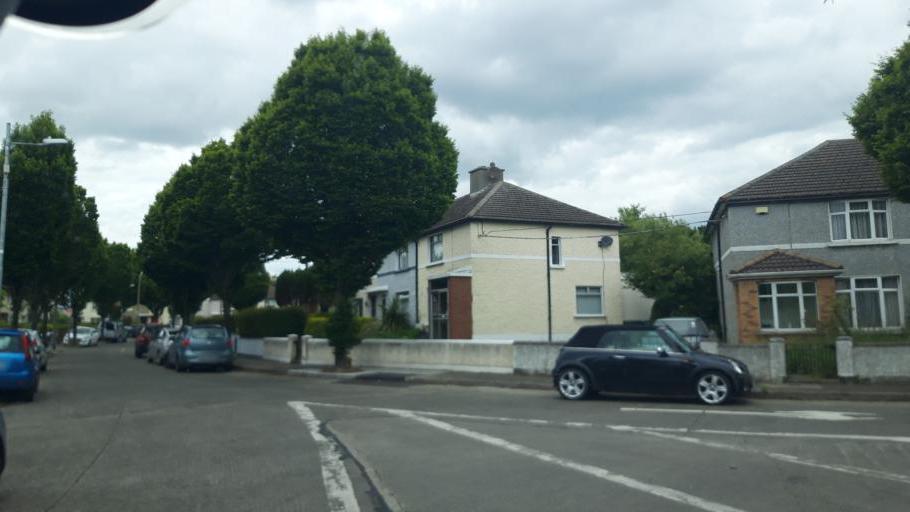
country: IE
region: Leinster
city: Dollymount
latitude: 53.3602
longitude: -6.1899
